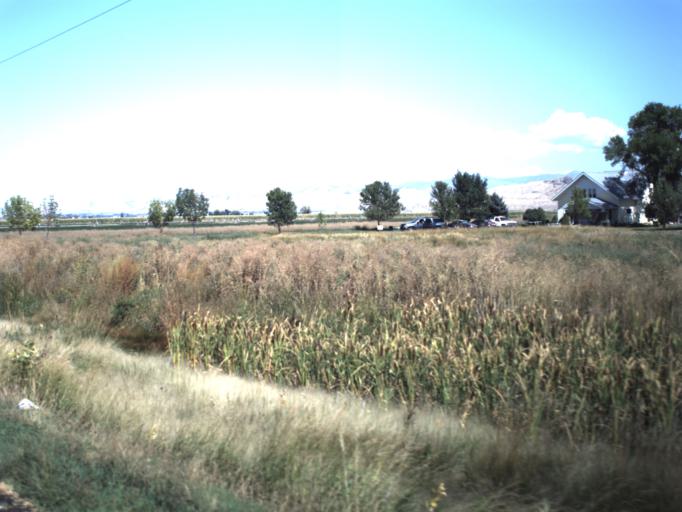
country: US
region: Utah
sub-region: Cache County
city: Lewiston
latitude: 41.9957
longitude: -111.8765
